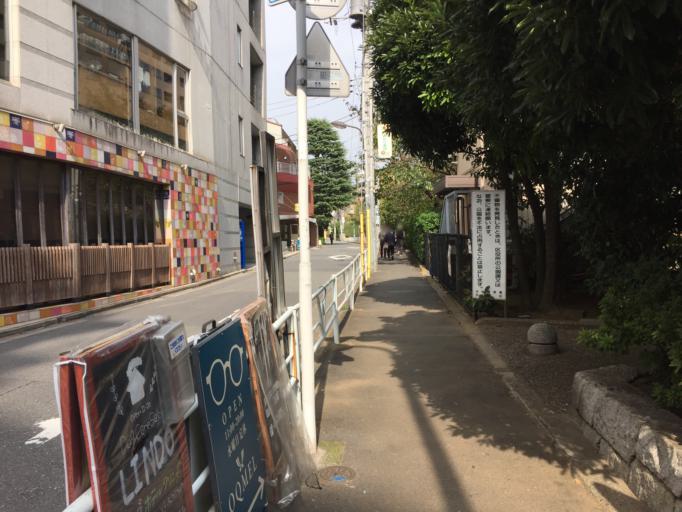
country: JP
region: Tokyo
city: Tokyo
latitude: 35.6479
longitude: 139.7220
